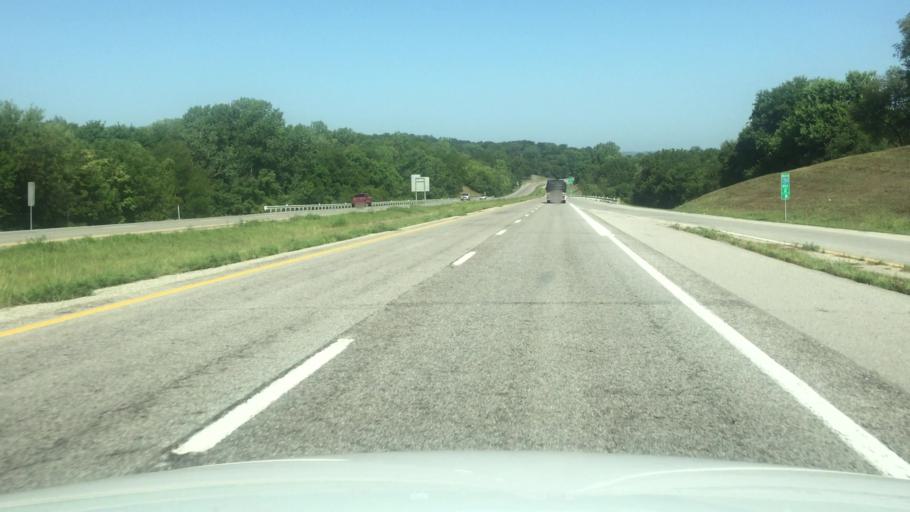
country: US
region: Missouri
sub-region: Buchanan County
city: Saint Joseph
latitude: 39.7232
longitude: -94.8361
